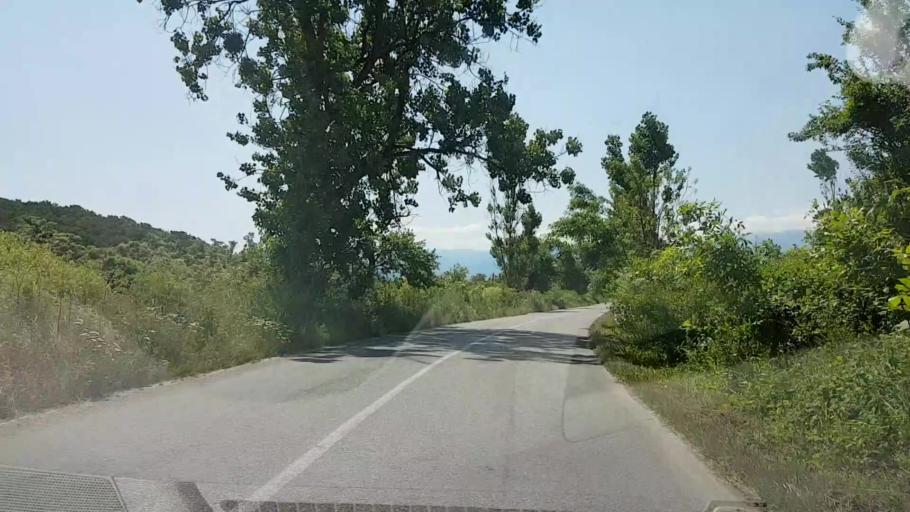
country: RO
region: Brasov
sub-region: Comuna Voila
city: Voila
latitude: 45.8524
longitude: 24.8318
